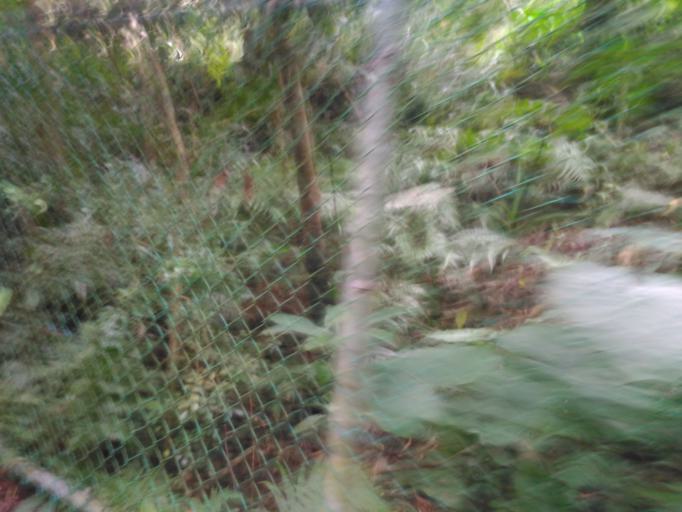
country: TW
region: Taipei
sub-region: Taipei
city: Banqiao
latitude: 24.9534
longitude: 121.4444
